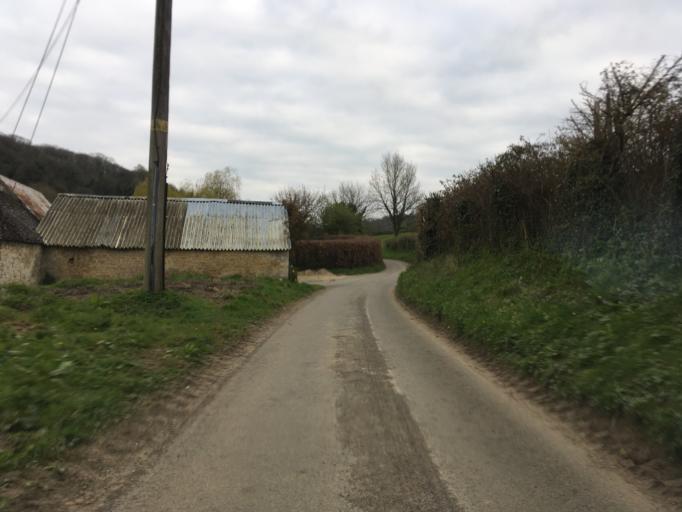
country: GB
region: England
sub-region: Gloucestershire
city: Wotton-under-Edge
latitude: 51.6024
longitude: -2.3121
